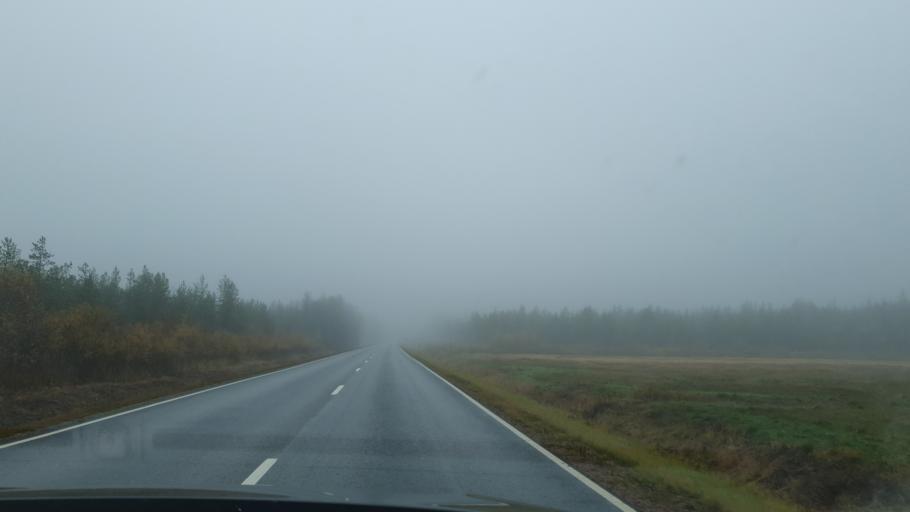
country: FI
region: Lapland
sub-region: Rovaniemi
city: Rovaniemi
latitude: 66.7984
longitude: 25.4145
